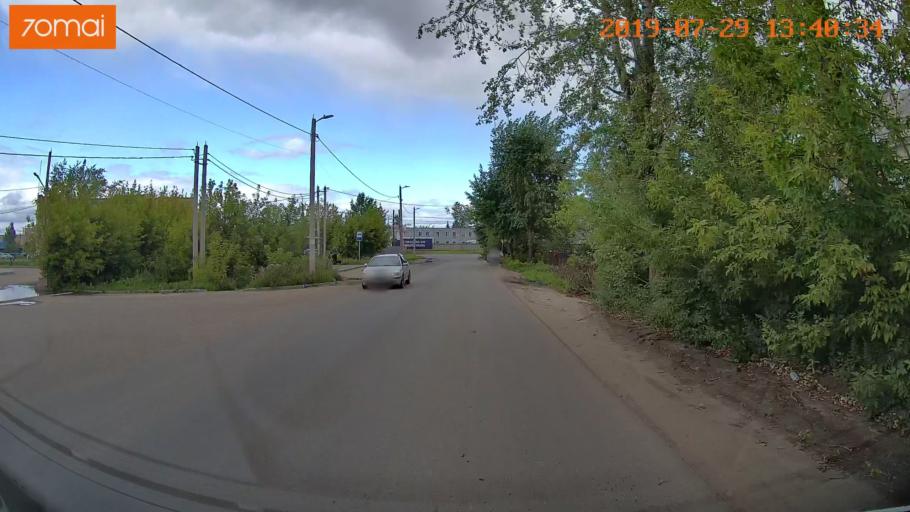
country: RU
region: Ivanovo
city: Novo-Talitsy
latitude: 56.9977
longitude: 40.9150
